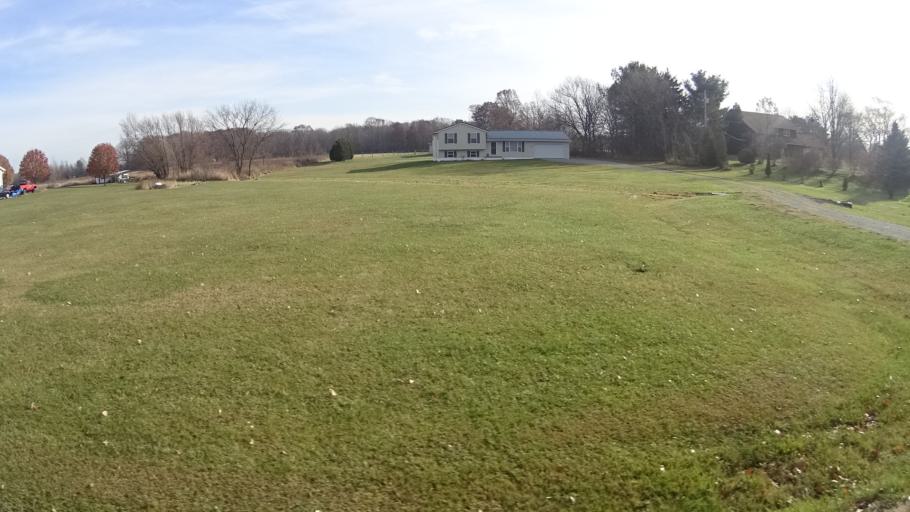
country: US
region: Ohio
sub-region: Lorain County
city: Grafton
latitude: 41.2031
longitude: -81.9738
